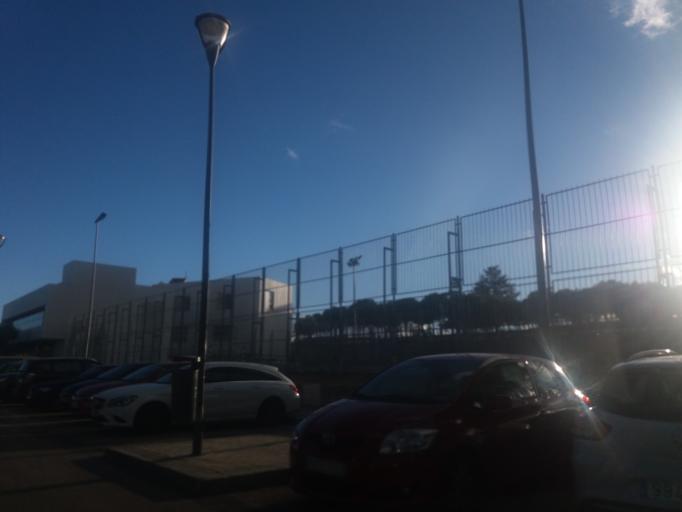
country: ES
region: Madrid
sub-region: Provincia de Madrid
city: Pozuelo de Alarcon
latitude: 40.4367
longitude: -3.8006
